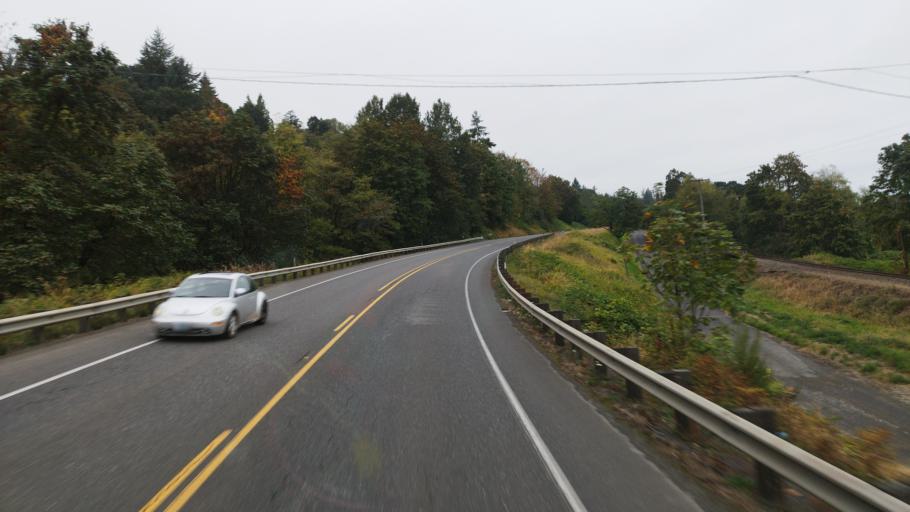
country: US
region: Washington
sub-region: Cowlitz County
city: Kalama
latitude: 45.9443
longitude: -122.8594
